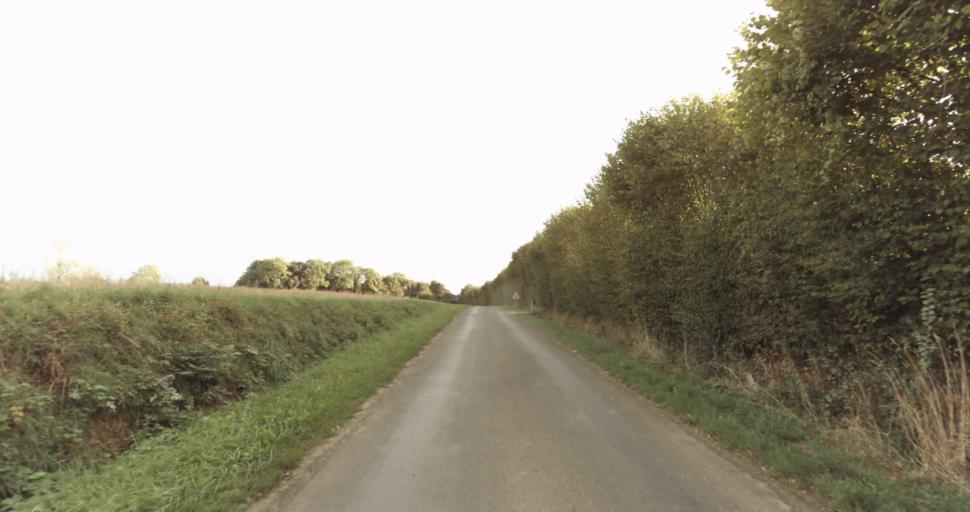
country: FR
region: Lower Normandy
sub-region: Departement de l'Orne
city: Sees
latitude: 48.6928
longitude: 0.2296
